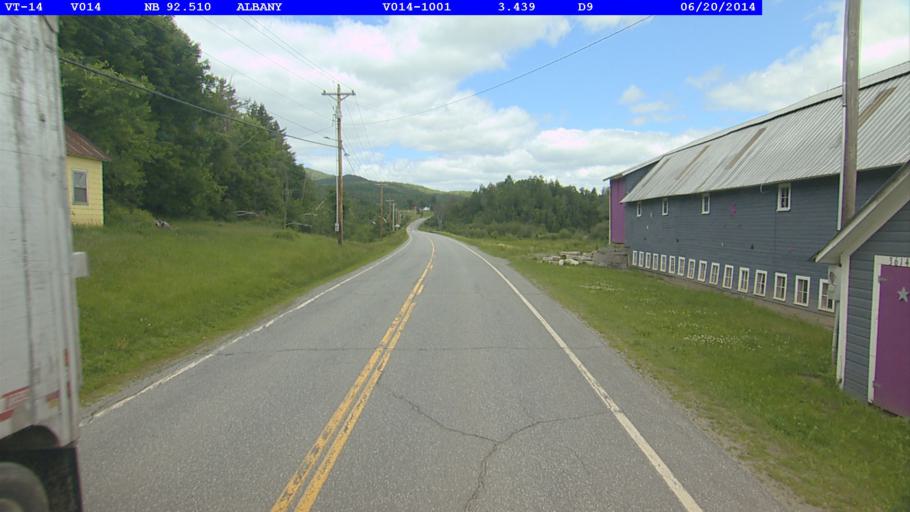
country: US
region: Vermont
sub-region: Caledonia County
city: Hardwick
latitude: 44.7483
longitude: -72.3686
